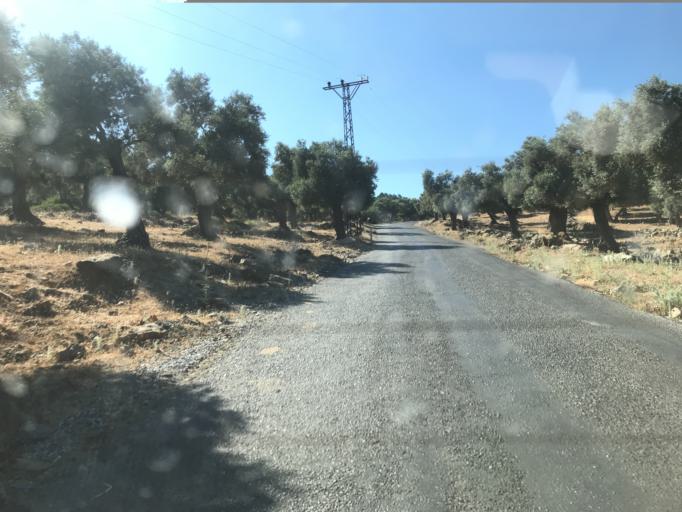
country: TR
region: Mugla
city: Selimiye
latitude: 37.3823
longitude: 27.4854
